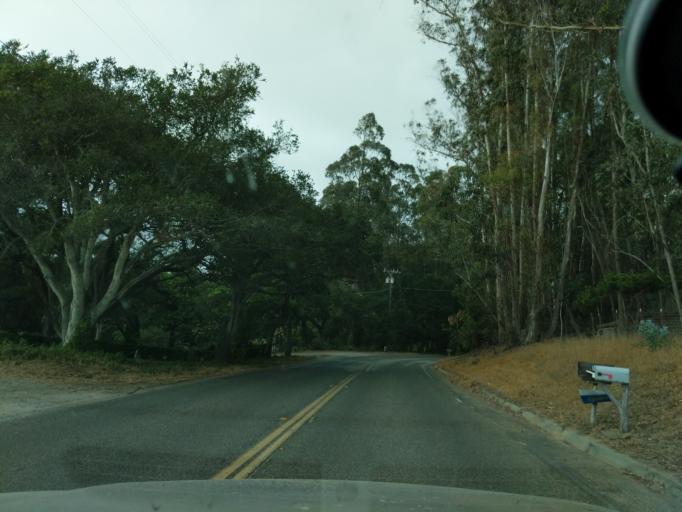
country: US
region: California
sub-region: Monterey County
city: Elkhorn
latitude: 36.8134
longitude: -121.7238
